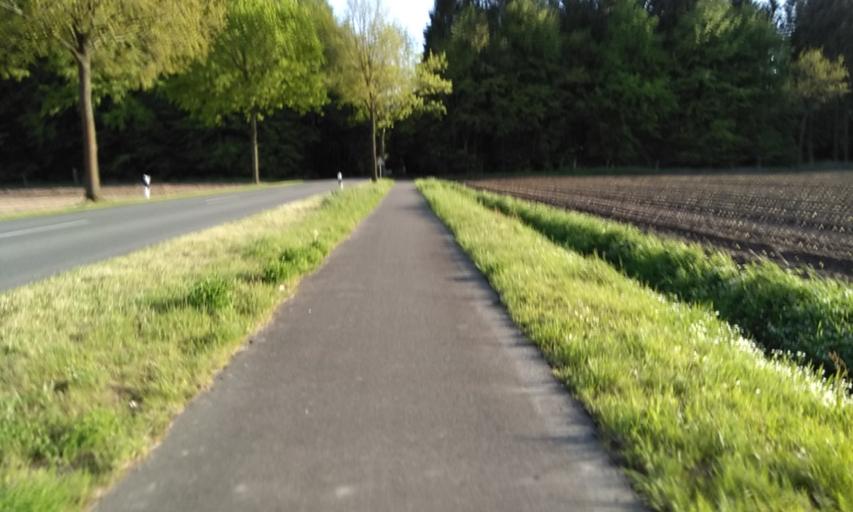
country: DE
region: Lower Saxony
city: Wohnste
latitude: 53.4012
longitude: 9.5411
